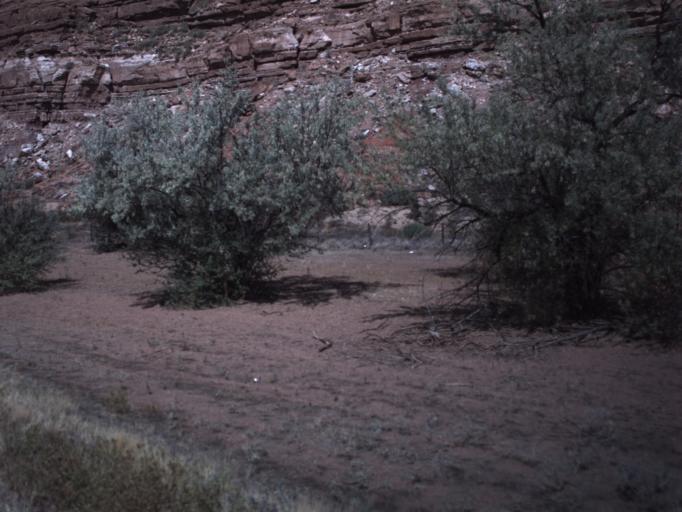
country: US
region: Utah
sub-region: San Juan County
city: Blanding
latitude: 37.2853
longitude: -109.5194
